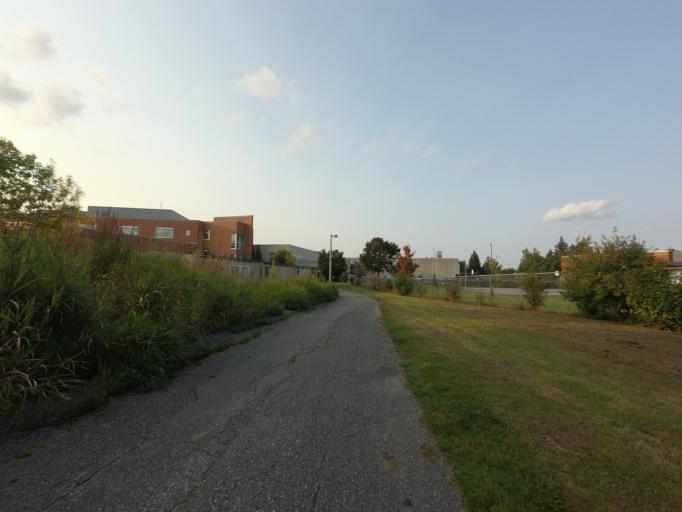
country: CA
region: Ontario
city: Bells Corners
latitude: 45.2788
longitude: -75.7615
